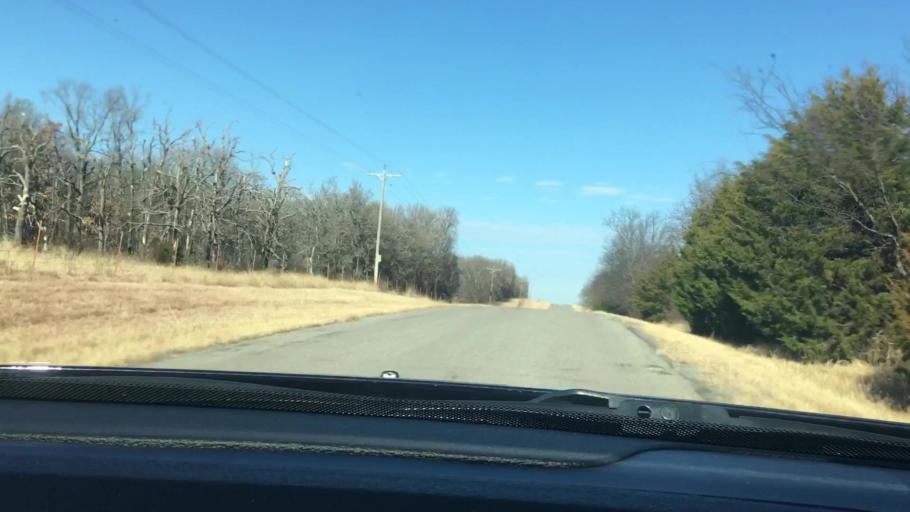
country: US
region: Oklahoma
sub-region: Garvin County
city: Wynnewood
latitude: 34.6677
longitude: -97.1254
